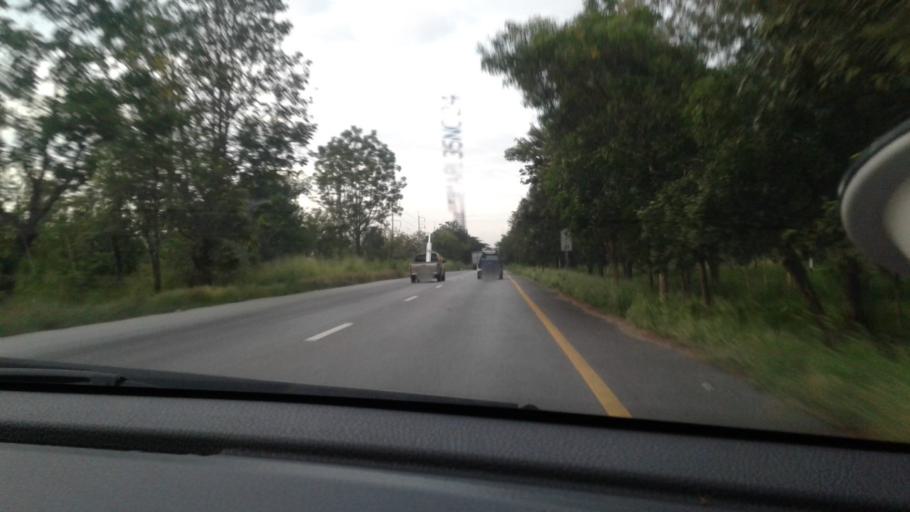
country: TH
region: Prachuap Khiri Khan
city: Hua Hin
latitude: 12.5559
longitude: 99.8715
